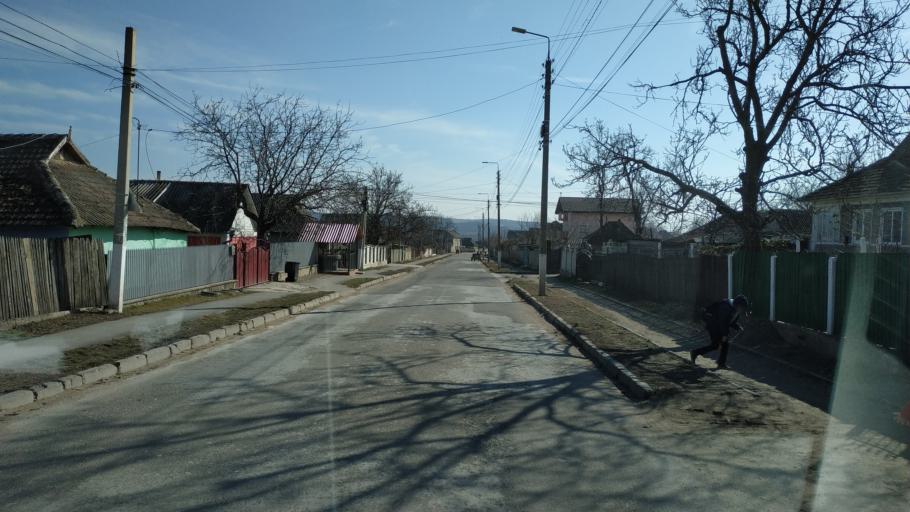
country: MD
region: Nisporeni
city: Nisporeni
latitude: 47.0779
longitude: 28.1683
